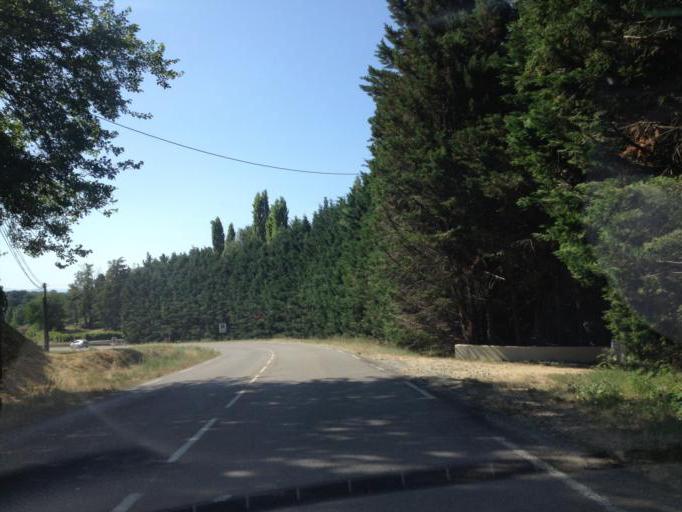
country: FR
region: Rhone-Alpes
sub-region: Departement de la Drome
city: Clerieux
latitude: 45.1200
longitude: 4.9650
